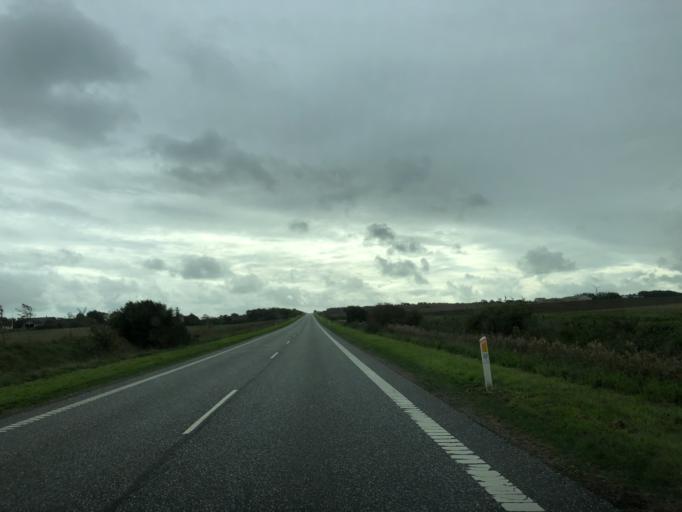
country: DK
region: North Denmark
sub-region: Thisted Kommune
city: Hurup
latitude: 56.7653
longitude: 8.4563
